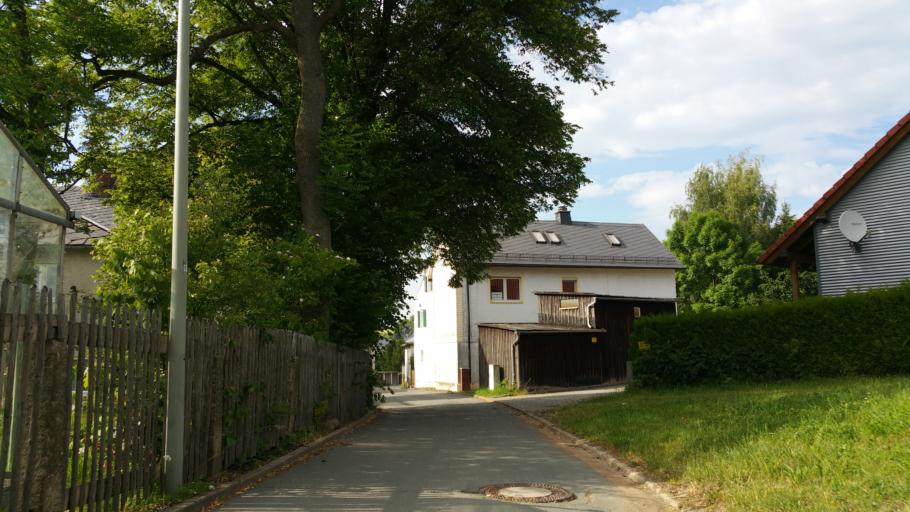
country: DE
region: Bavaria
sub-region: Upper Franconia
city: Schwarzenbach an der Saale
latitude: 50.2077
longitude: 11.9687
